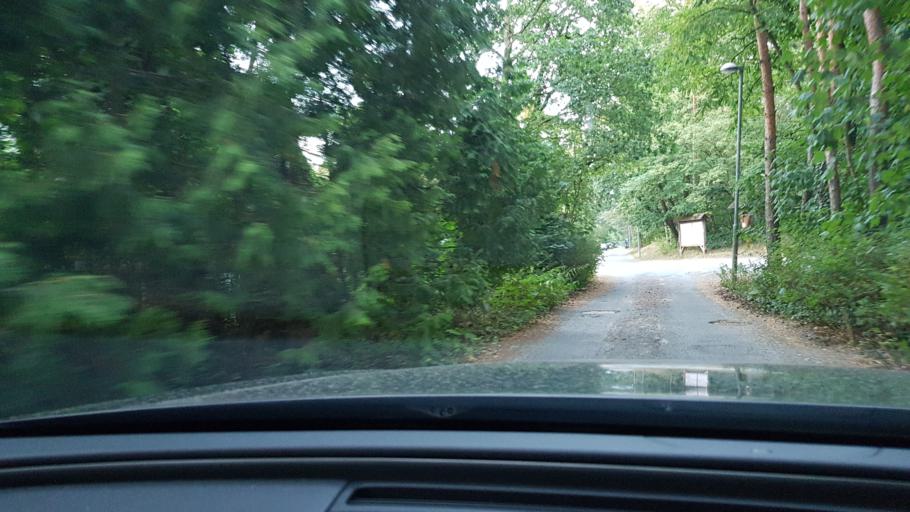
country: DE
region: Berlin
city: Friedrichshagen
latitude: 52.4747
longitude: 13.6194
